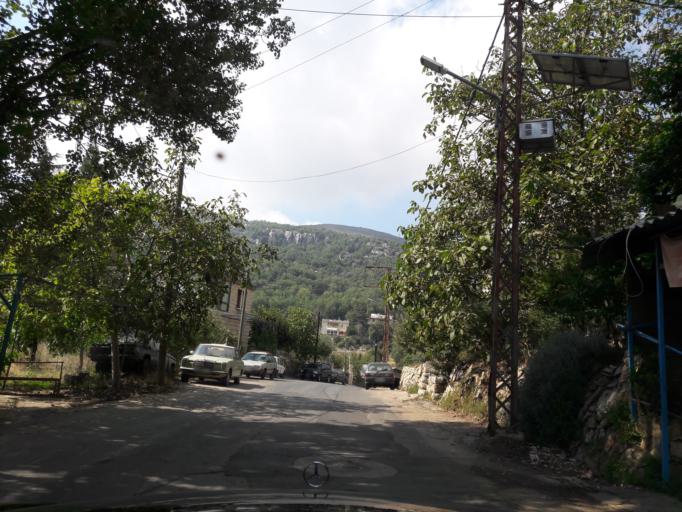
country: LB
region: Mont-Liban
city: Djounie
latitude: 33.9616
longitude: 35.7801
